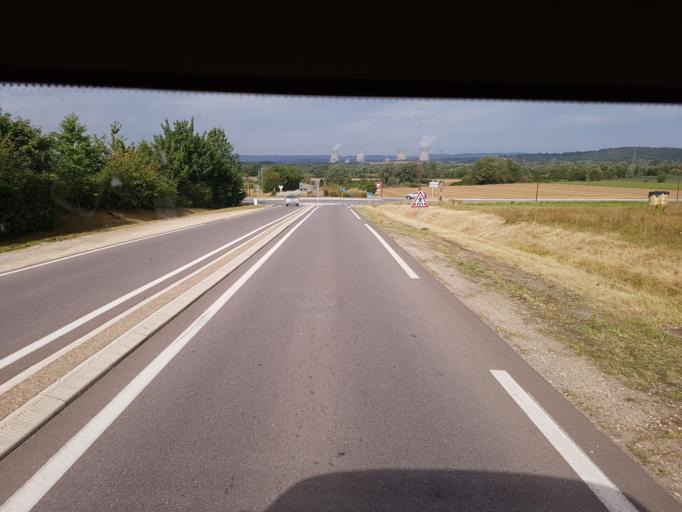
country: FR
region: Lorraine
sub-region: Departement de la Moselle
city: Koenigsmacker
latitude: 49.4061
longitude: 6.2991
